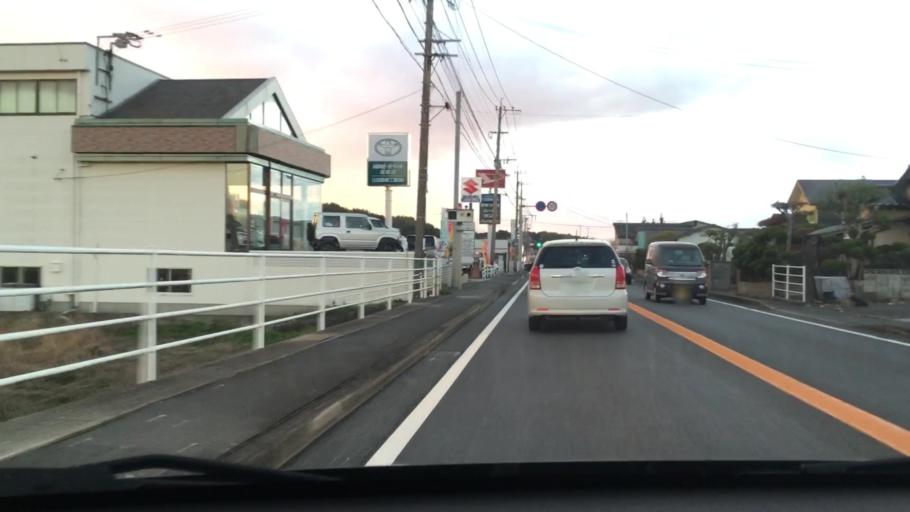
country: JP
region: Fukuoka
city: Shiida
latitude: 33.6322
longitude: 131.0809
